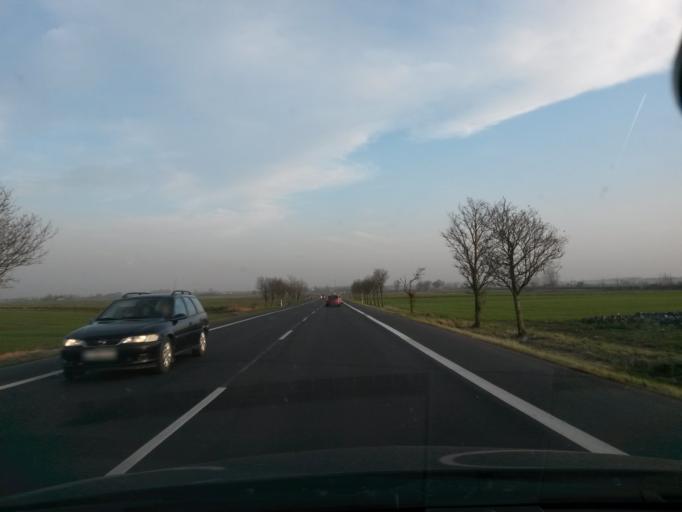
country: PL
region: Lodz Voivodeship
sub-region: Powiat wielunski
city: Czarnozyly
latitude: 51.2504
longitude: 18.5124
